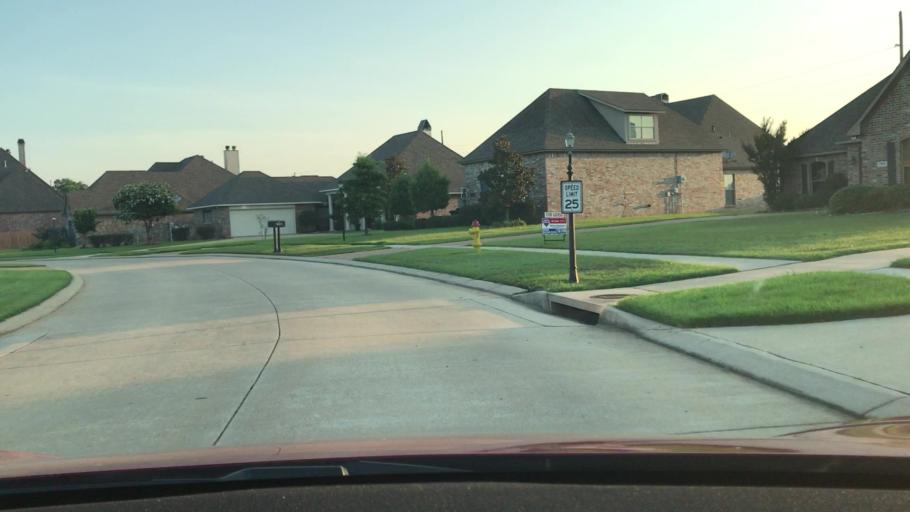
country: US
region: Louisiana
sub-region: Bossier Parish
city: Bossier City
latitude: 32.3947
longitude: -93.7046
